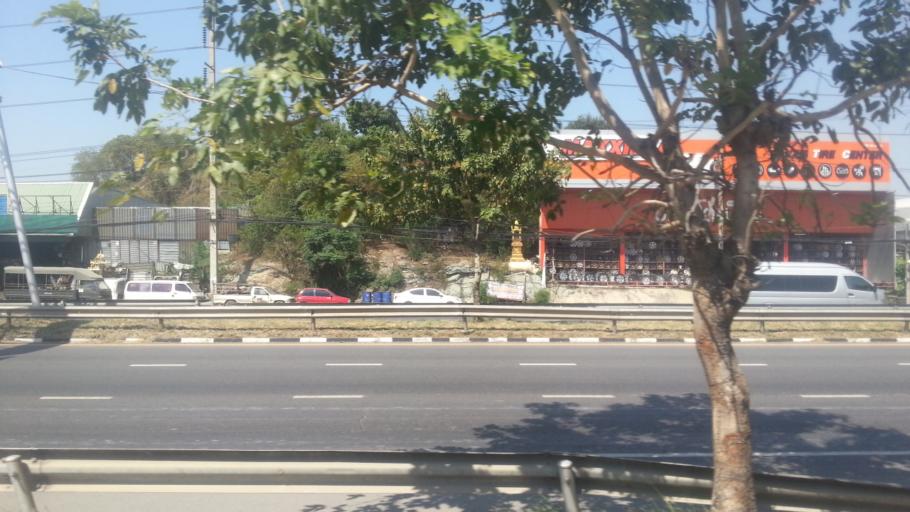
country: TH
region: Sara Buri
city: Saraburi
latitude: 14.5204
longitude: 100.9250
